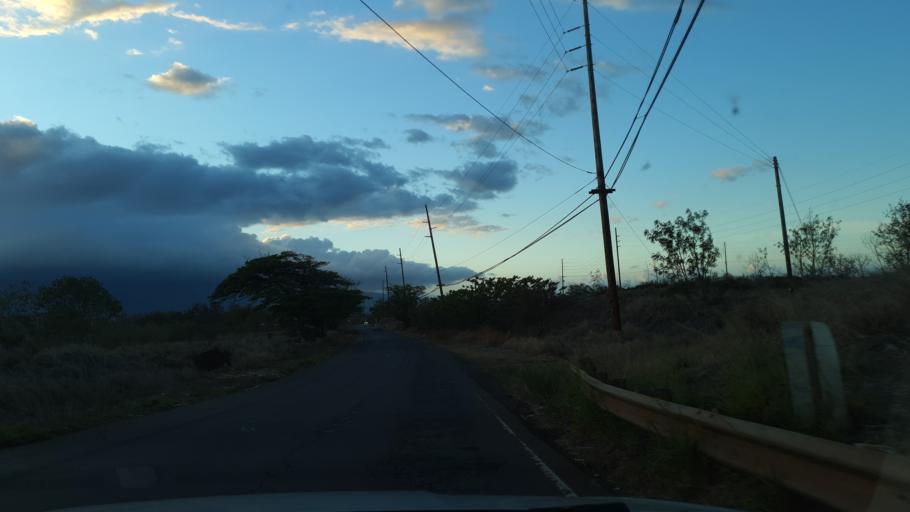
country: US
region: Hawaii
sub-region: Maui County
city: Kahului
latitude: 20.8704
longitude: -156.4372
